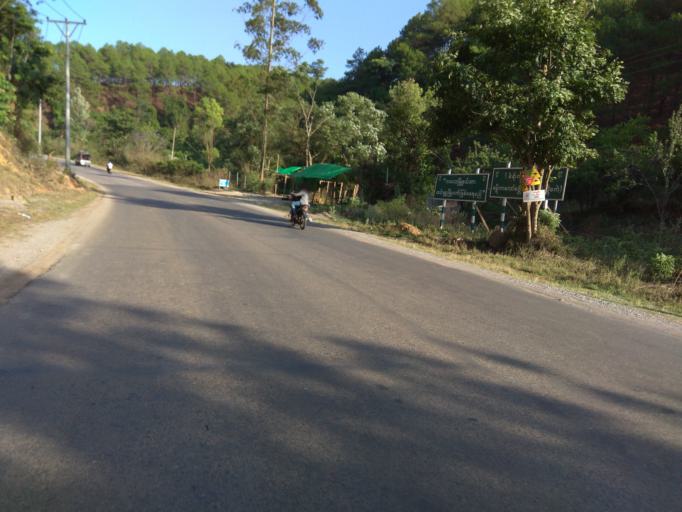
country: MM
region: Shan
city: Taunggyi
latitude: 20.6334
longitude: 96.5838
